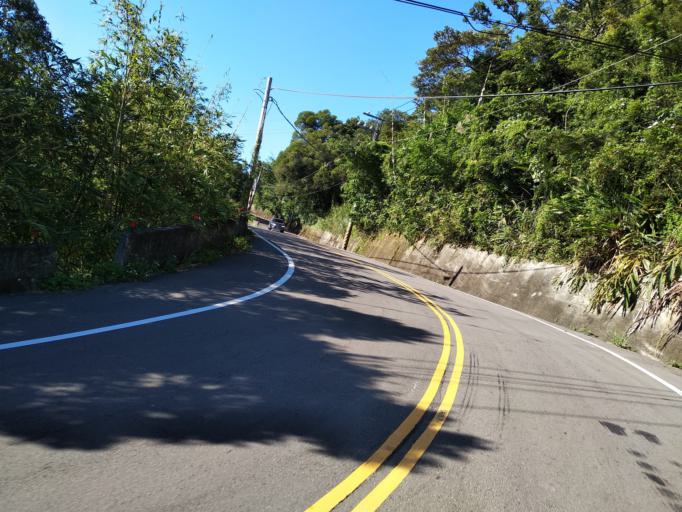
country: TW
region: Taiwan
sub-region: Hsinchu
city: Zhubei
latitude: 24.8675
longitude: 121.0976
